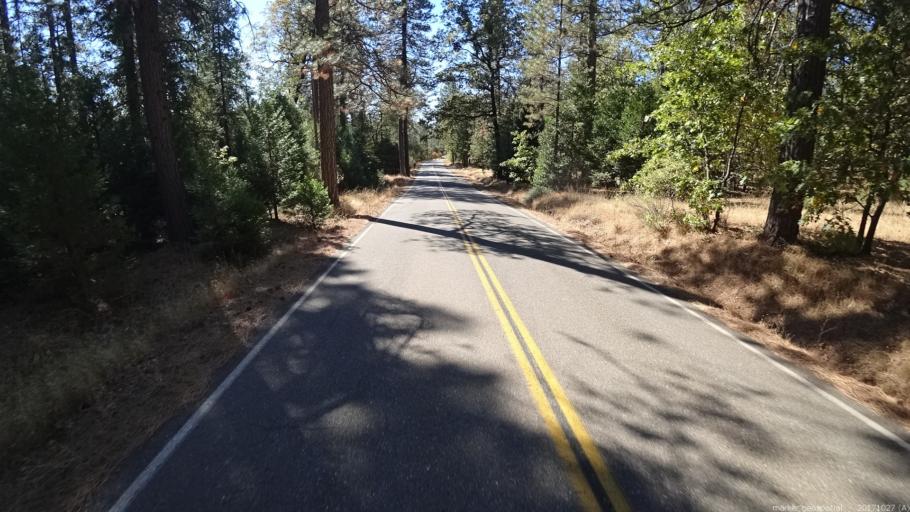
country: US
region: California
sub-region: Shasta County
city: Shingletown
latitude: 40.6960
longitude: -122.0023
